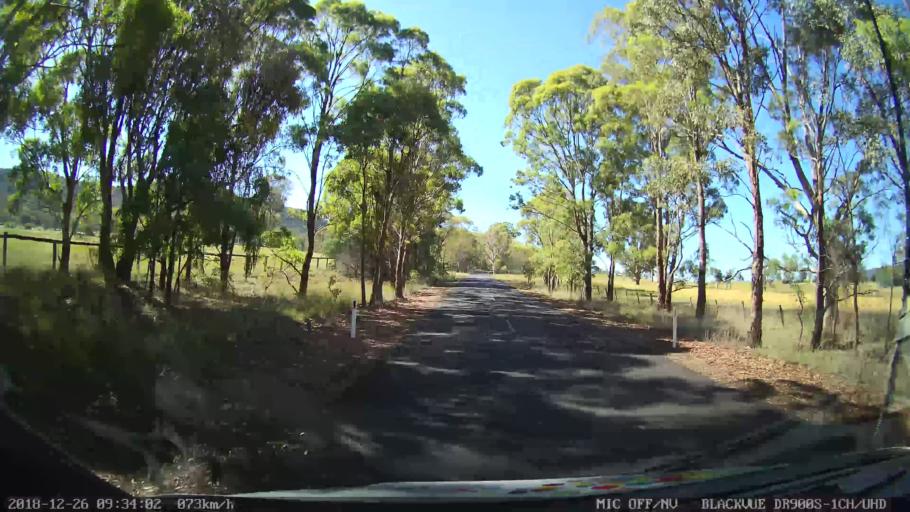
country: AU
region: New South Wales
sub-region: Mid-Western Regional
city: Kandos
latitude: -32.9010
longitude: 150.0368
